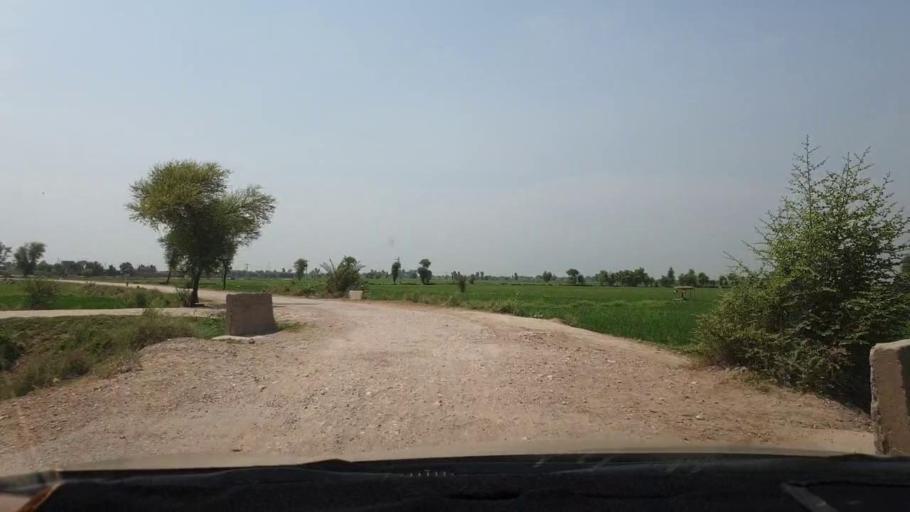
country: PK
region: Sindh
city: Naudero
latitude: 27.6367
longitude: 68.2734
